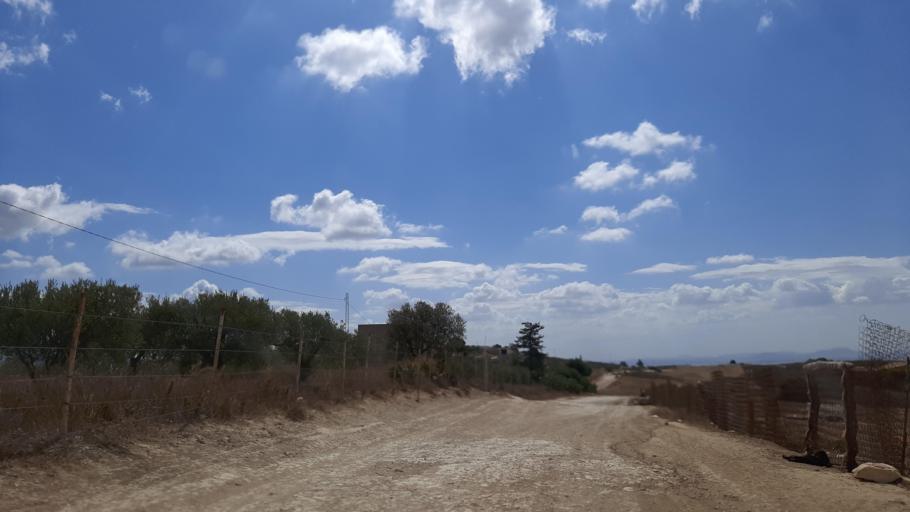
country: TN
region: Zaghwan
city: Zaghouan
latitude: 36.4876
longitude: 10.1786
